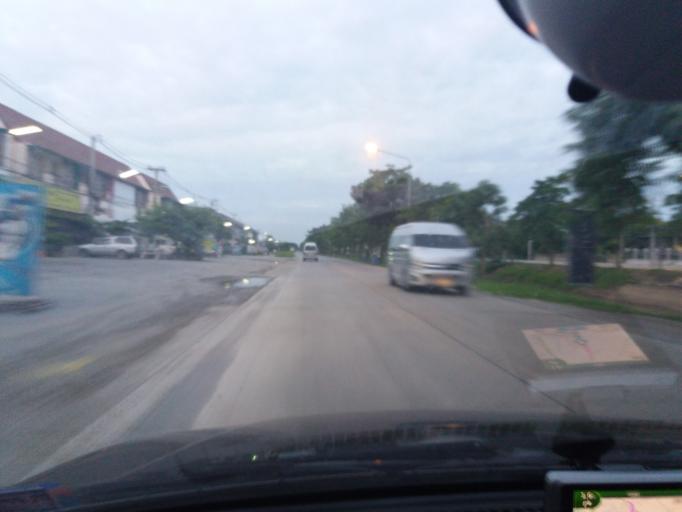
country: TH
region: Suphan Buri
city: Sam Chuk
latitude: 14.7506
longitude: 100.0930
